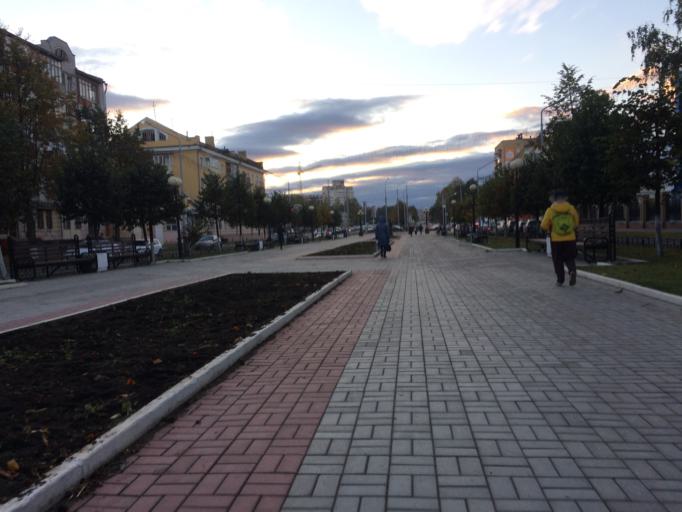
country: RU
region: Mariy-El
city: Yoshkar-Ola
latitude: 56.6399
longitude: 47.8739
